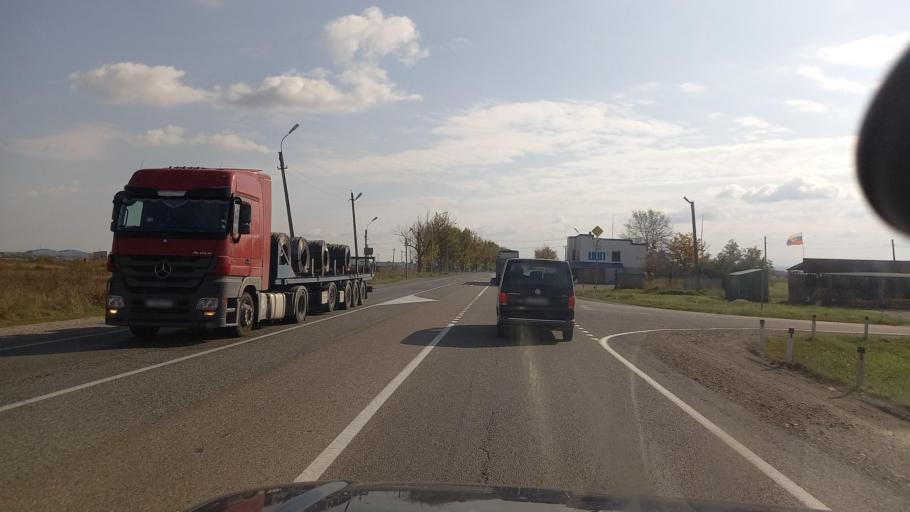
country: RU
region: Krasnodarskiy
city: Abinsk
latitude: 44.8723
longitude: 38.1227
